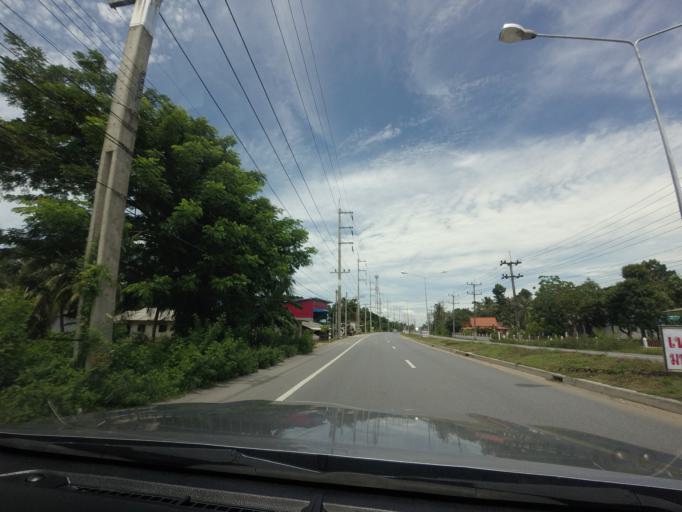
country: TH
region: Songkhla
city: Krasae Sin
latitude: 7.6107
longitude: 100.3987
